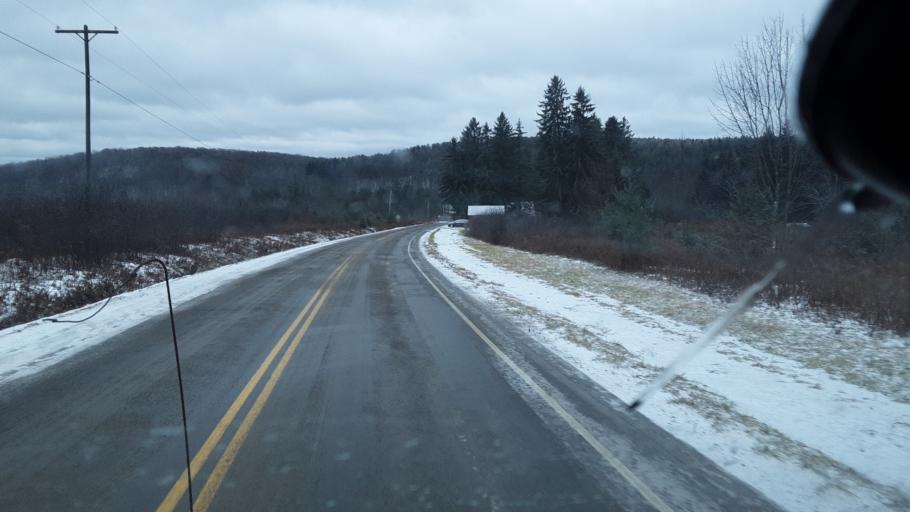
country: US
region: New York
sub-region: Allegany County
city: Friendship
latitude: 42.2362
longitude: -78.1426
